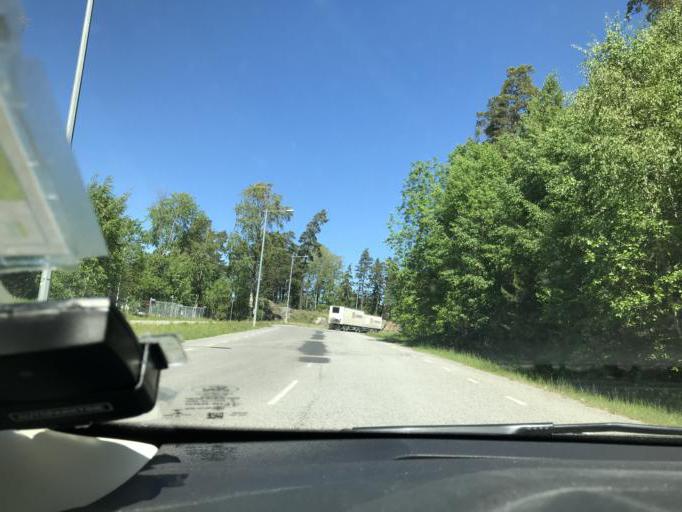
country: SE
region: Stockholm
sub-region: Botkyrka Kommun
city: Tumba
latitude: 59.2120
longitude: 17.8427
